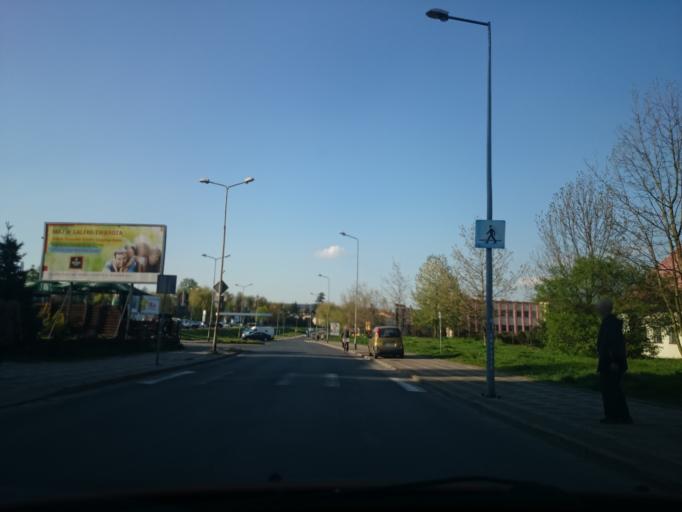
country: PL
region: Lower Silesian Voivodeship
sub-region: Powiat klodzki
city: Klodzko
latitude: 50.4373
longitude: 16.6416
